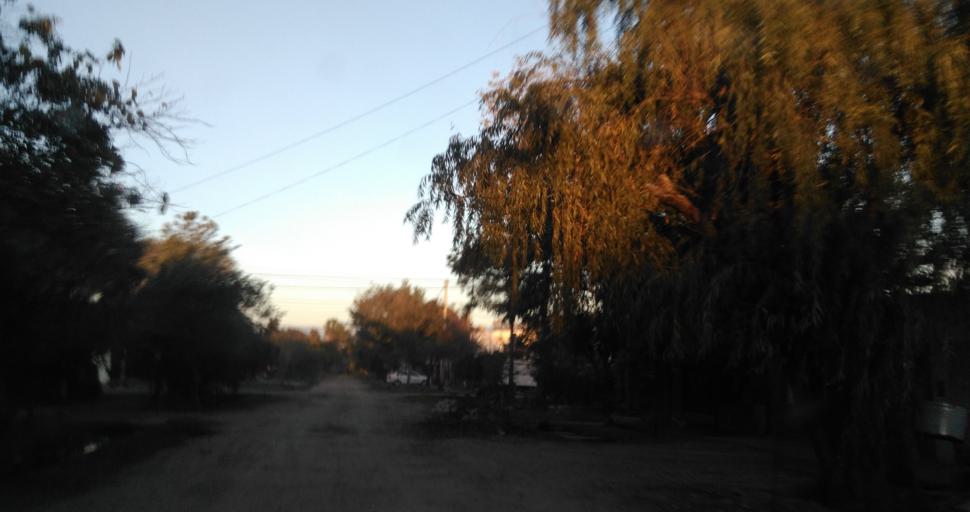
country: AR
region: Chaco
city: Fontana
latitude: -27.4380
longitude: -59.0200
